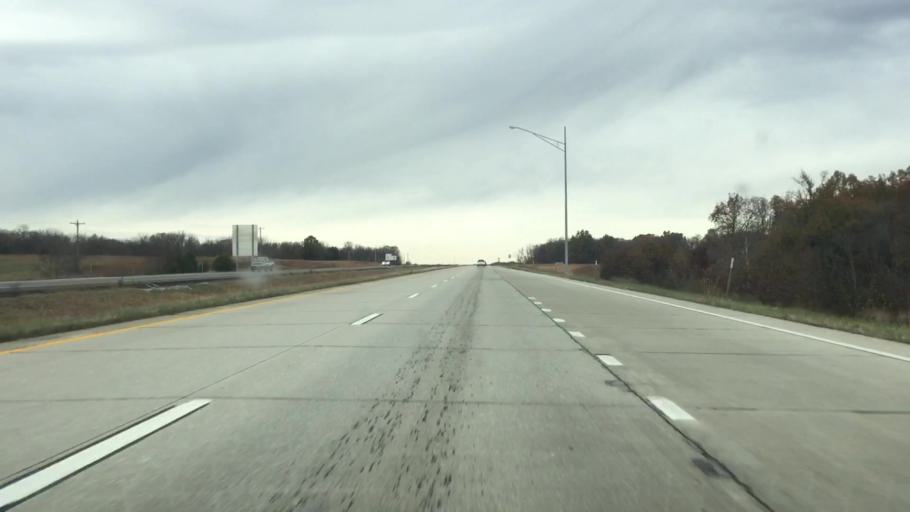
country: US
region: Missouri
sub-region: Saint Clair County
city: Osceola
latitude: 38.0437
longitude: -93.6830
